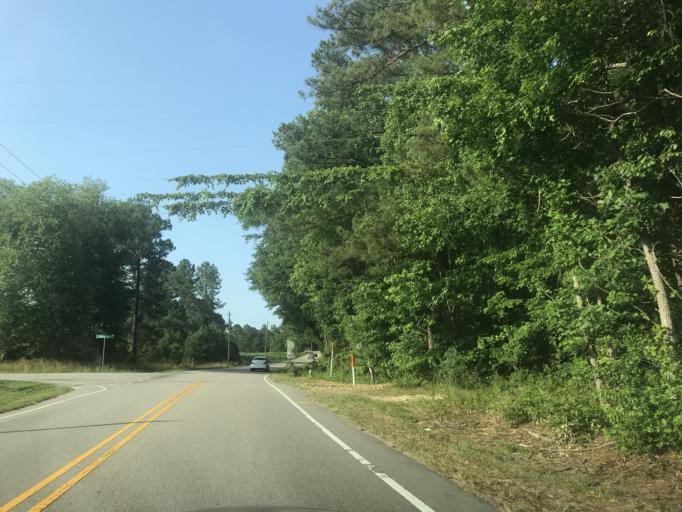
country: US
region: North Carolina
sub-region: Wake County
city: Knightdale
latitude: 35.8574
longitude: -78.4959
